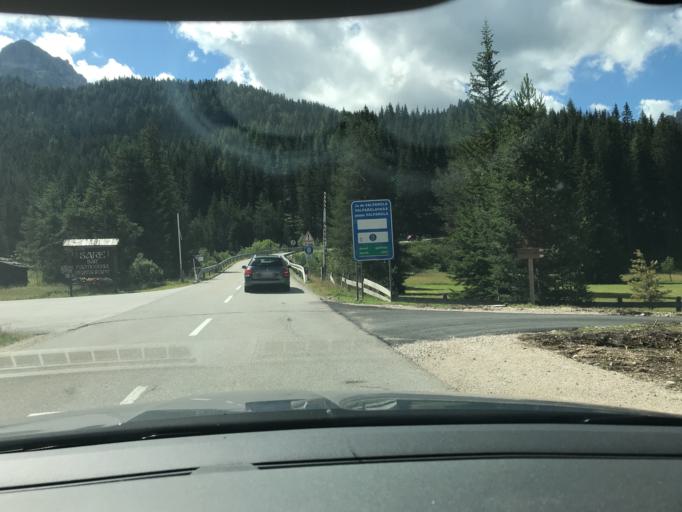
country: IT
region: Veneto
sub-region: Provincia di Belluno
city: Livinallongo del Col di Lana
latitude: 46.5532
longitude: 11.9683
